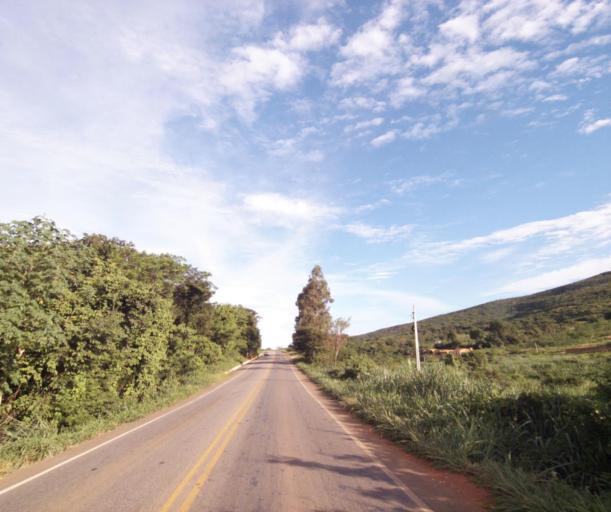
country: BR
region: Bahia
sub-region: Caetite
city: Caetite
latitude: -14.0651
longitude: -42.4746
